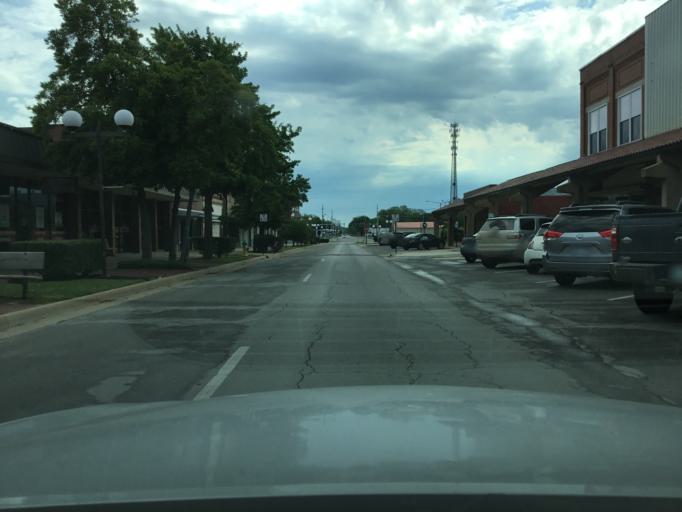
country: US
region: Kansas
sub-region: Montgomery County
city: Coffeyville
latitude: 37.0361
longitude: -95.6170
